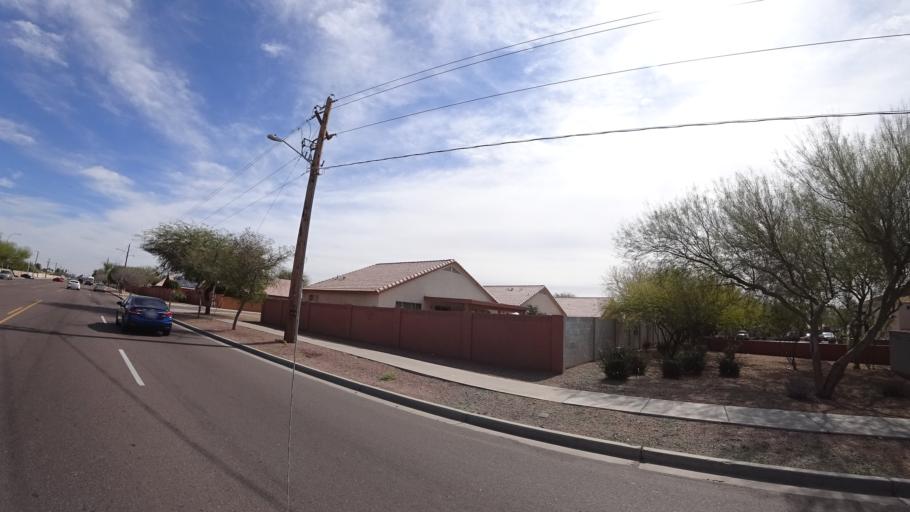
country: US
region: Arizona
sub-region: Maricopa County
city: Tolleson
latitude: 33.4797
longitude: -112.2528
